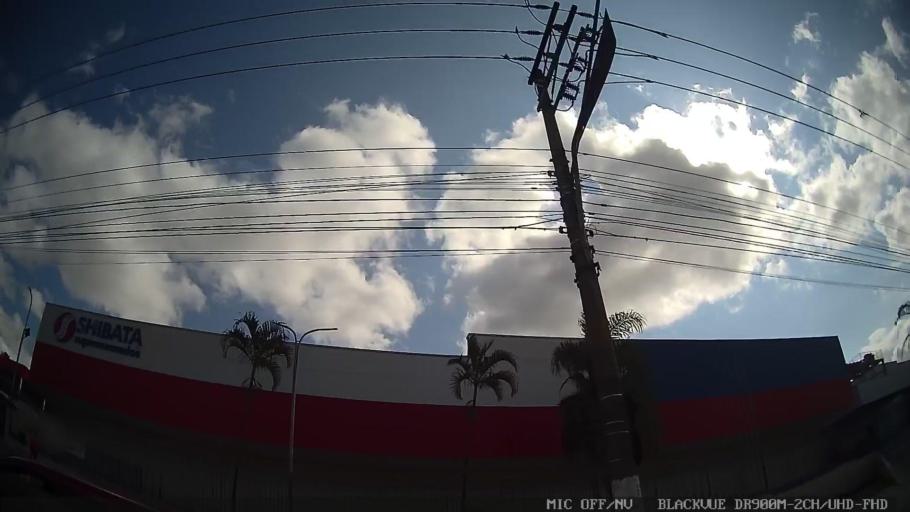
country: BR
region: Sao Paulo
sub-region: Guarulhos
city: Guarulhos
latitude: -23.4902
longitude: -46.4631
